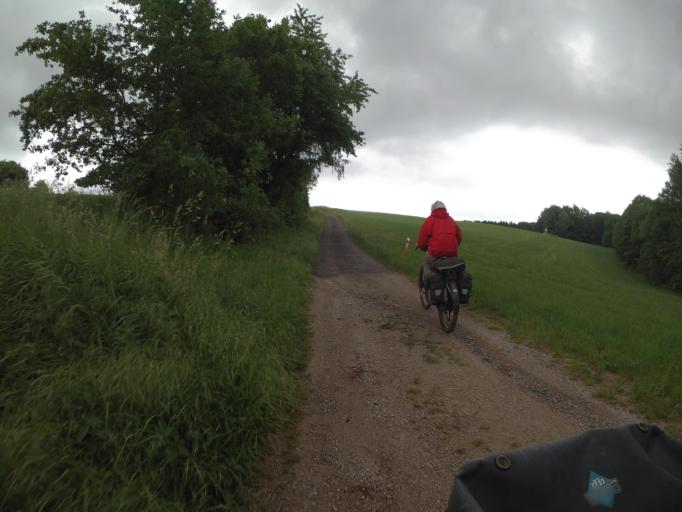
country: DE
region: Rheinland-Pfalz
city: Obersimten
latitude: 49.1683
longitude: 7.5988
